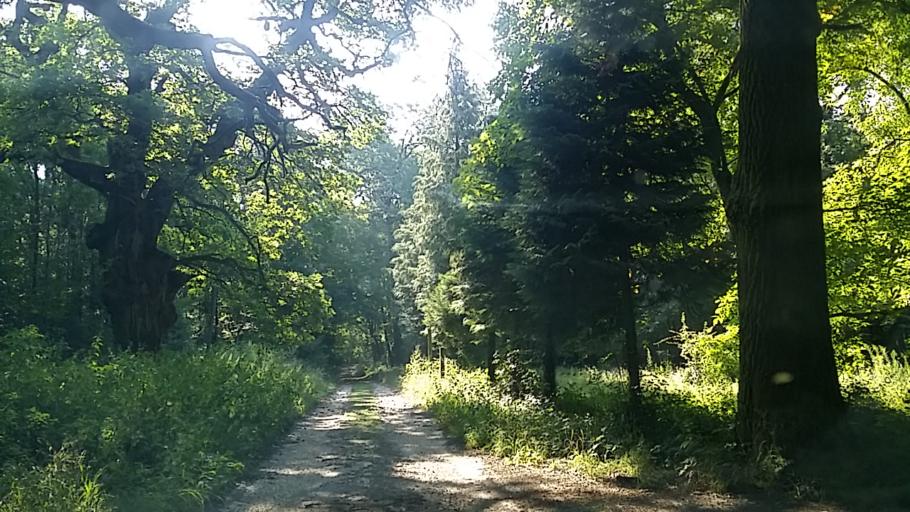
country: HU
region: Komarom-Esztergom
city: Tatabanya
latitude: 47.5927
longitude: 18.4329
